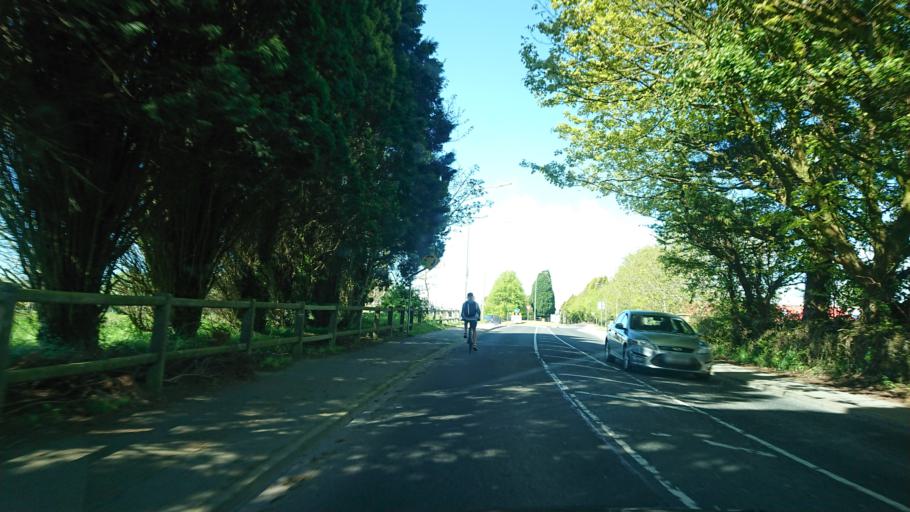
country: IE
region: Munster
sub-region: Waterford
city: Waterford
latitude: 52.2541
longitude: -7.1472
